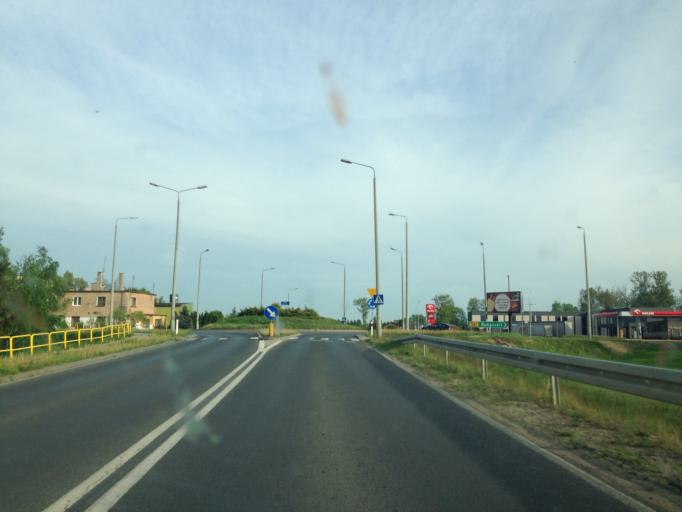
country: PL
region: Kujawsko-Pomorskie
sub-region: Powiat wabrzeski
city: Wabrzezno
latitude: 53.2779
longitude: 18.9308
